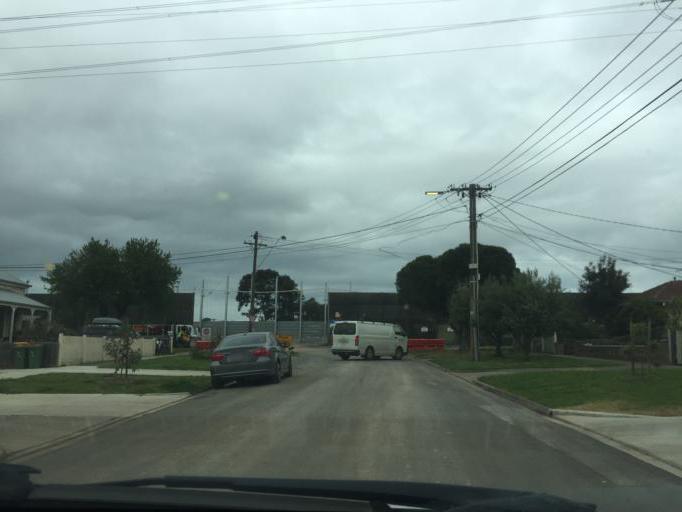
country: AU
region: Victoria
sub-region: Hobsons Bay
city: South Kingsville
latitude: -37.8239
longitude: 144.8764
